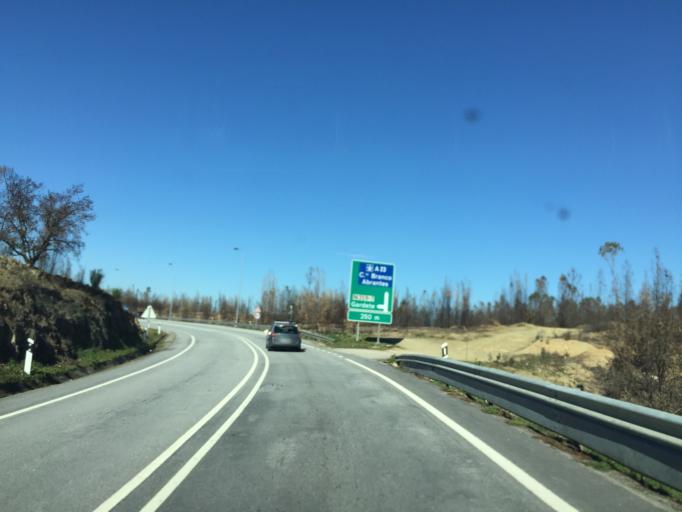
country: PT
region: Portalegre
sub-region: Nisa
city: Nisa
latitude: 39.5552
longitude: -7.7940
